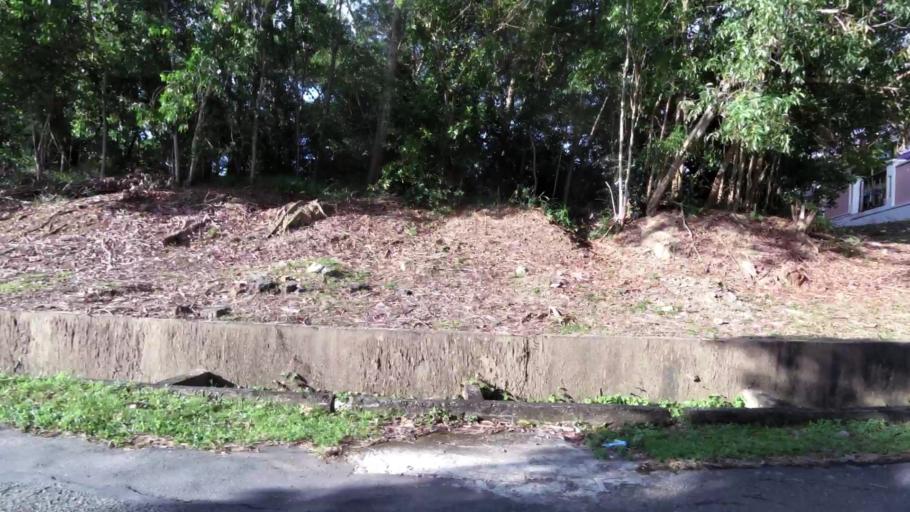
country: BN
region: Brunei and Muara
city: Bandar Seri Begawan
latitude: 4.9722
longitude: 114.9842
